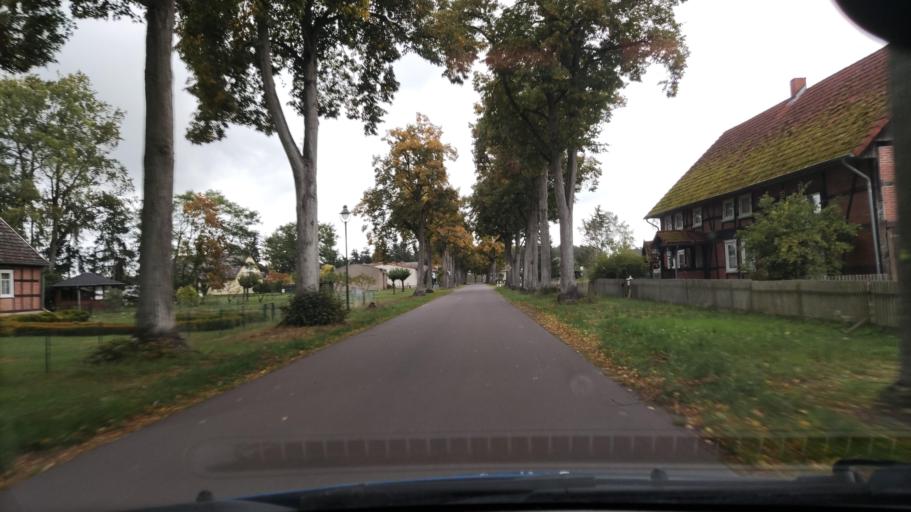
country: DE
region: Saxony-Anhalt
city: Luftkurort Arendsee
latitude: 52.9575
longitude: 11.5477
